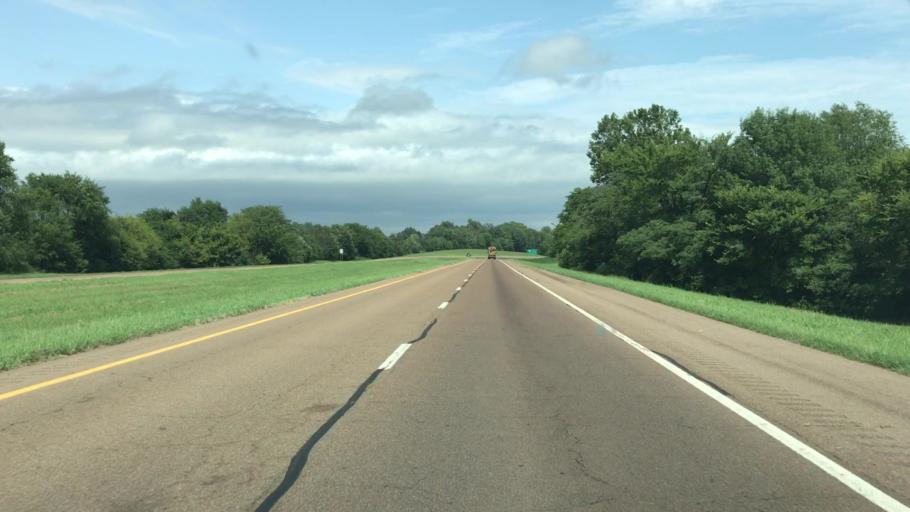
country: US
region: Tennessee
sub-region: Obion County
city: South Fulton
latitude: 36.4925
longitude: -88.9185
